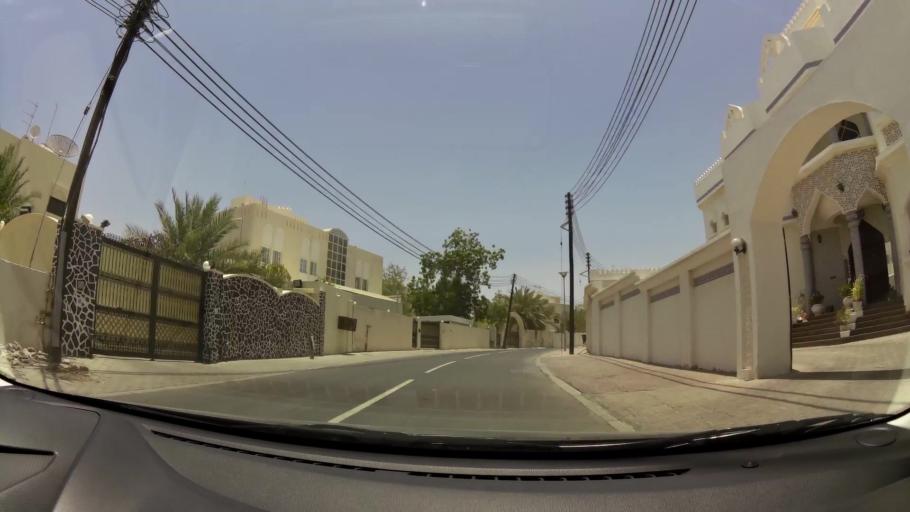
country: OM
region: Muhafazat Masqat
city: Bawshar
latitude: 23.6036
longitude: 58.4626
